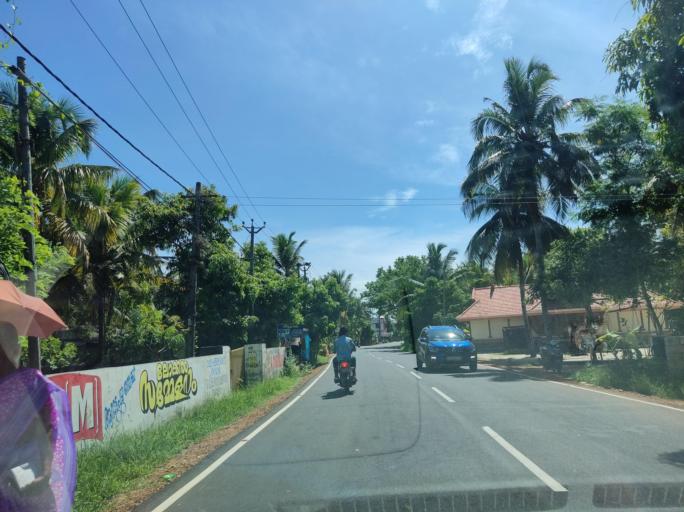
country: IN
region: Kerala
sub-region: Alappuzha
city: Kayankulam
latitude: 9.1657
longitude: 76.4525
